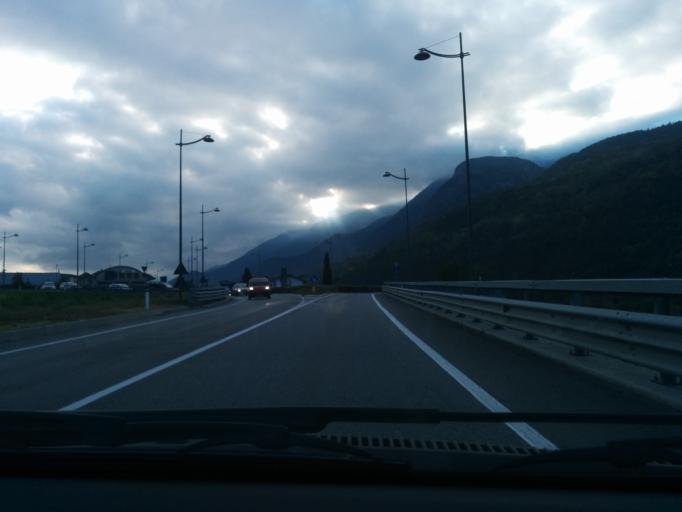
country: IT
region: Aosta Valley
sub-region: Valle d'Aosta
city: Nus
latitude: 45.7388
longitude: 7.4579
